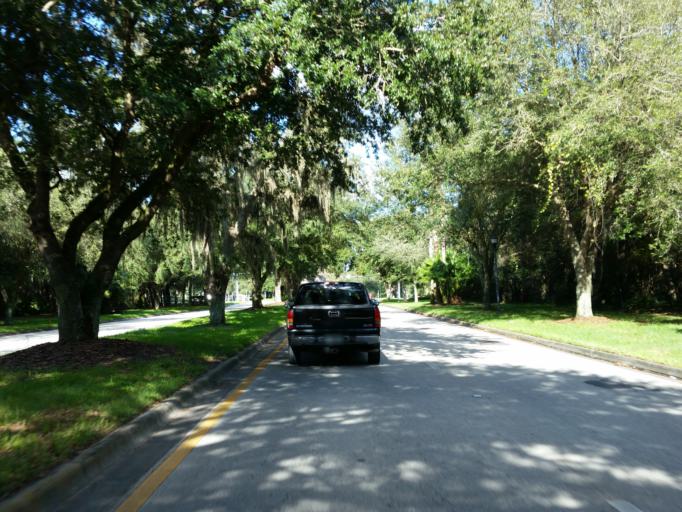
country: US
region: Florida
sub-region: Hillsborough County
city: Fish Hawk
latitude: 27.8518
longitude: -82.2321
